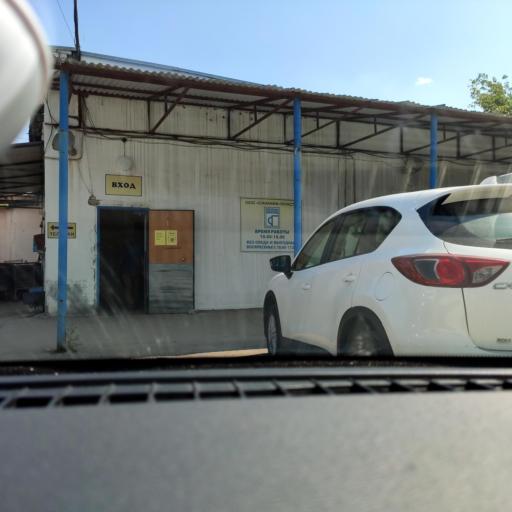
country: RU
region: Samara
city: Samara
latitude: 53.1797
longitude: 50.1470
